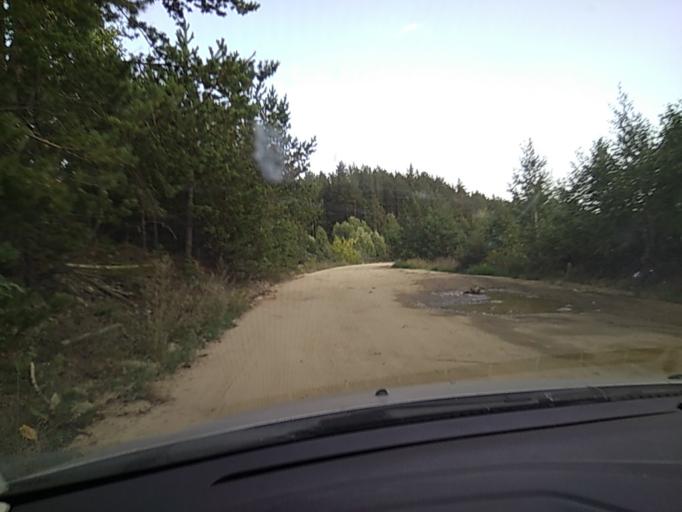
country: RU
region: Chelyabinsk
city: Kyshtym
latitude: 55.6840
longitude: 60.5705
